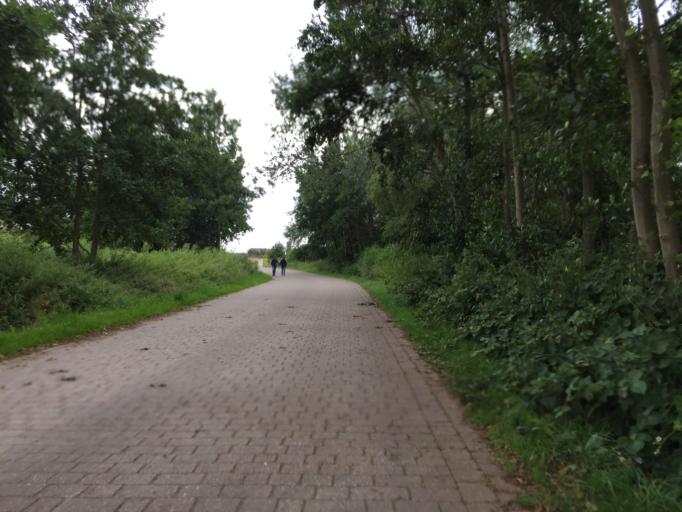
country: DE
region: Mecklenburg-Vorpommern
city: Hiddensee
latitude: 54.5294
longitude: 13.0859
